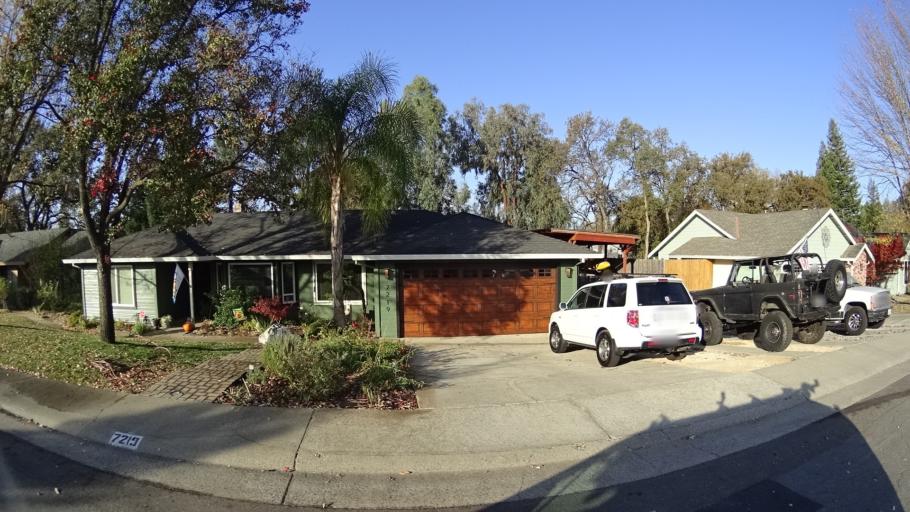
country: US
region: California
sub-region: Sacramento County
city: Citrus Heights
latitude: 38.6975
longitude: -121.2608
